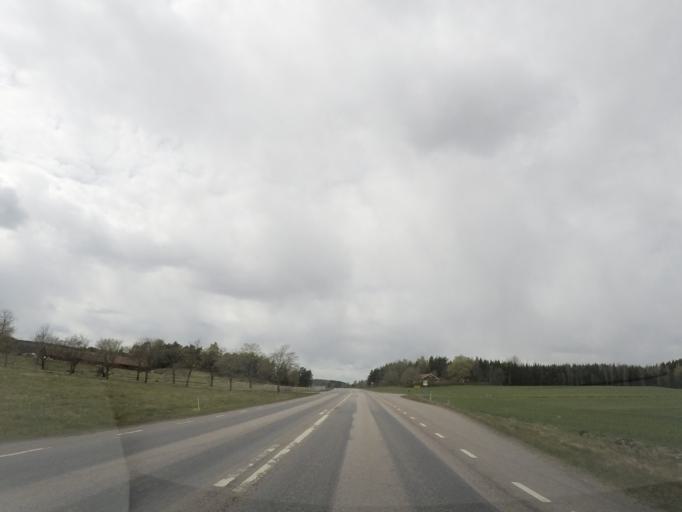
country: SE
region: Soedermanland
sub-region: Nykopings Kommun
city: Olstorp
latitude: 58.7442
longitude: 16.6960
